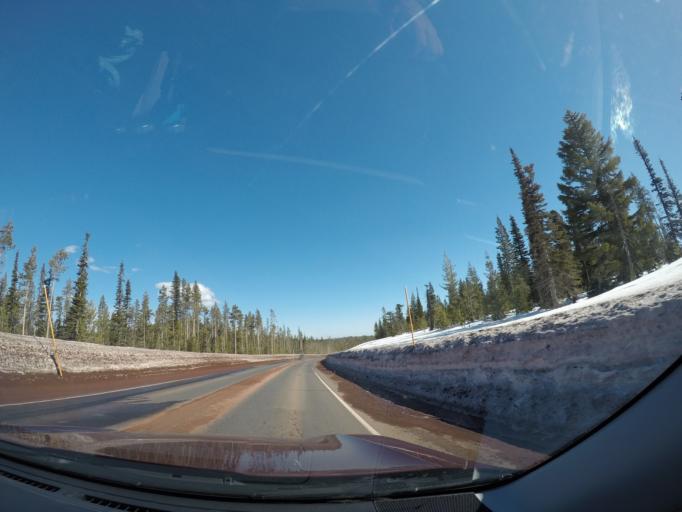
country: US
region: Oregon
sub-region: Deschutes County
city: Sunriver
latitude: 43.9846
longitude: -121.5787
